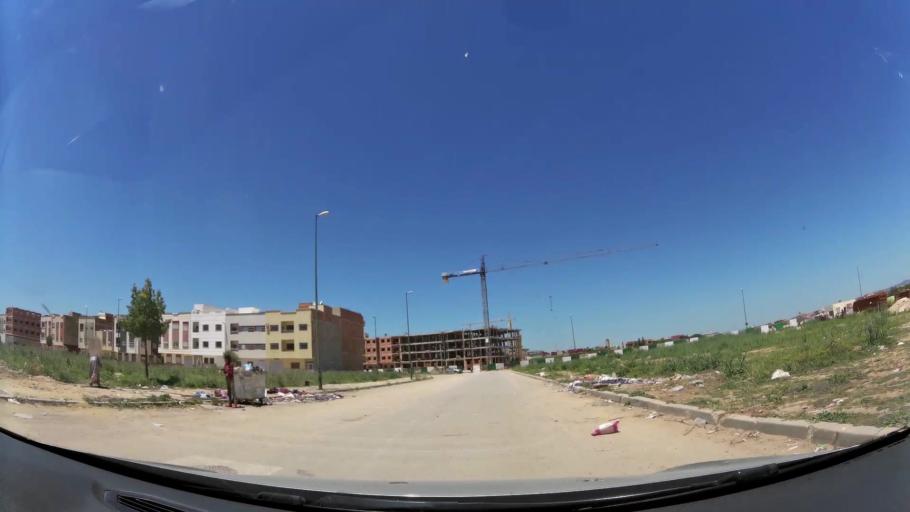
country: MA
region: Meknes-Tafilalet
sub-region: Meknes
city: Meknes
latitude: 33.8677
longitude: -5.5666
